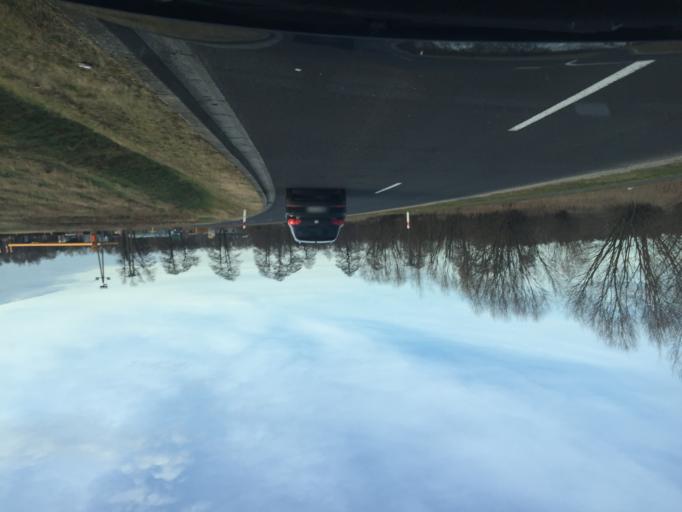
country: DE
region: Brandenburg
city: Forst
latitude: 51.7624
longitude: 14.6696
